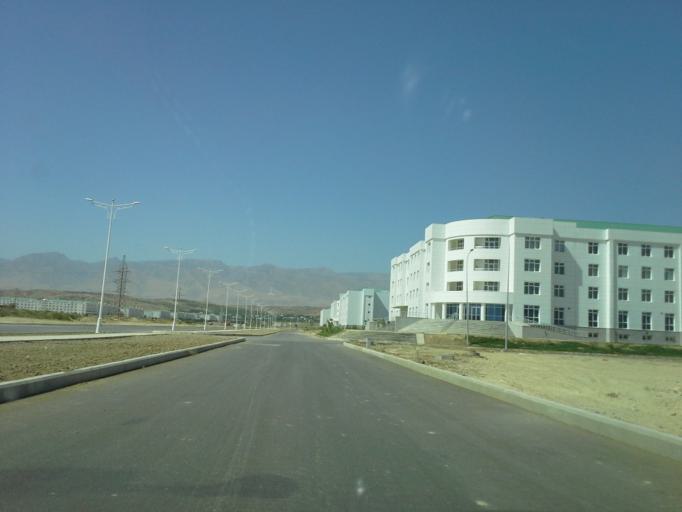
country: TM
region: Ahal
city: Ashgabat
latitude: 37.9757
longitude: 58.3325
